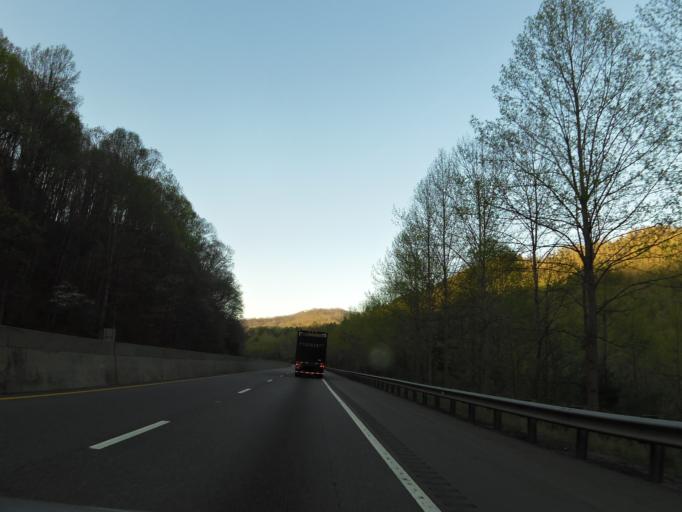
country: US
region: North Carolina
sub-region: Haywood County
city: Cove Creek
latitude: 35.6334
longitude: -82.9929
